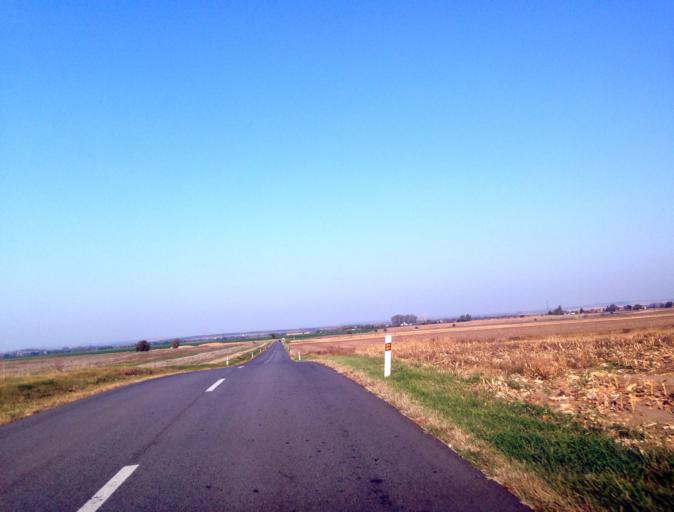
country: SK
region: Nitriansky
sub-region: Okres Komarno
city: Hurbanovo
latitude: 47.9086
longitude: 18.2867
